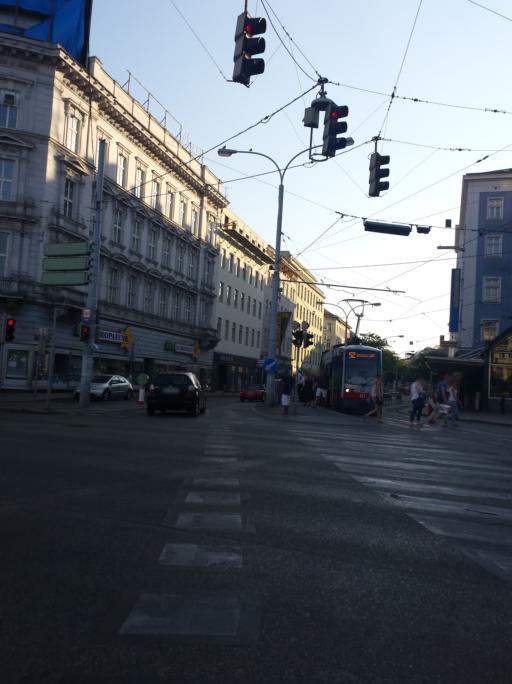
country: AT
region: Vienna
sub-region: Wien Stadt
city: Vienna
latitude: 48.1958
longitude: 16.3391
